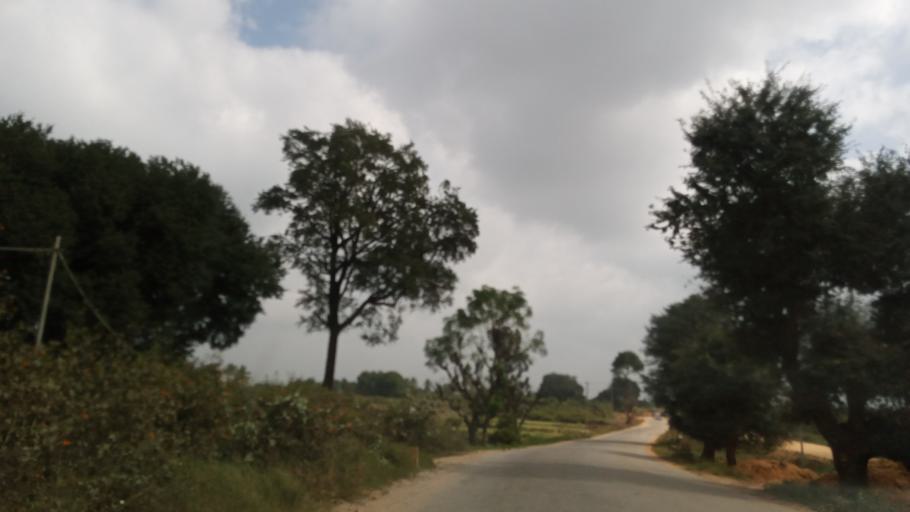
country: IN
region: Karnataka
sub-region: Kolar
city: Srinivaspur
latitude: 13.4451
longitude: 78.2344
